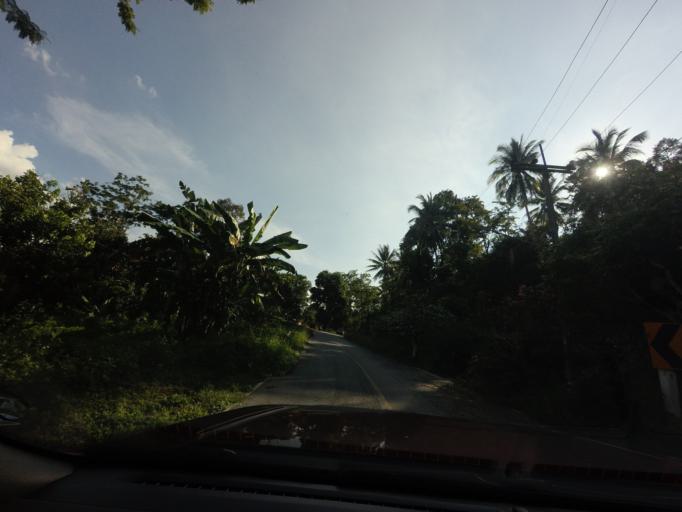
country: TH
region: Yala
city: Than To
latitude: 6.0876
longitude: 101.3259
